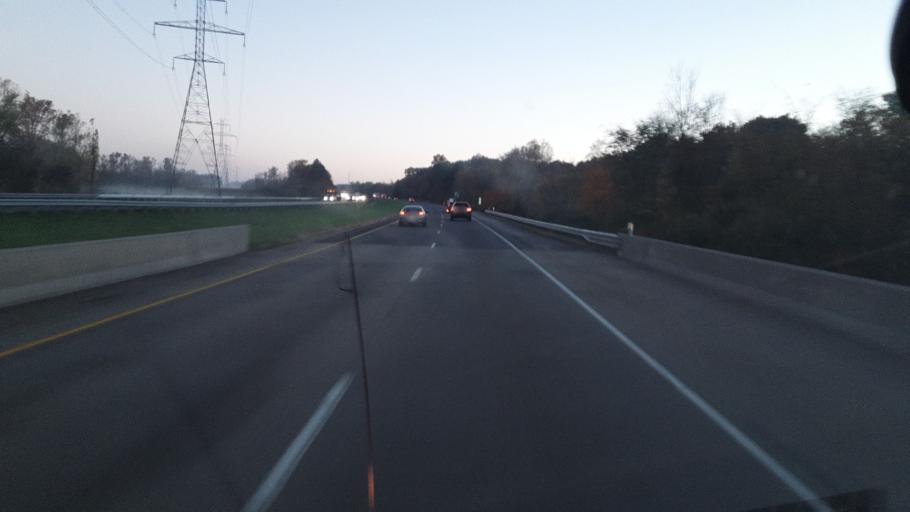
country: US
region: Indiana
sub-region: Allen County
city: Huntertown
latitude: 41.2362
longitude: -85.0938
